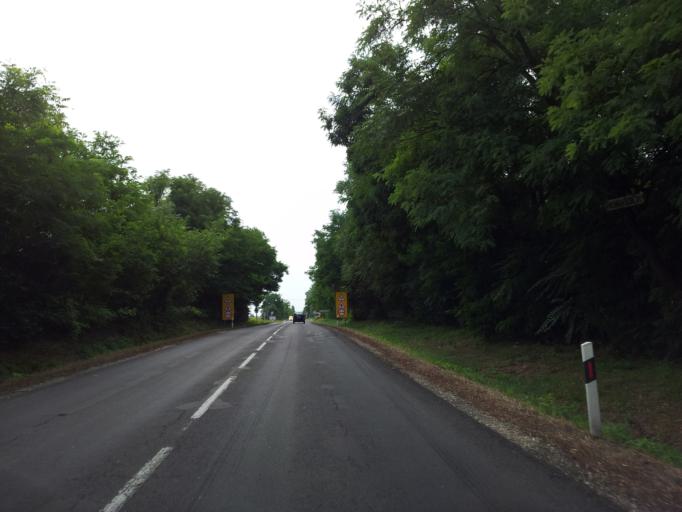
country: HU
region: Pest
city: Kiskunlachaza
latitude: 47.2366
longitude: 19.0207
